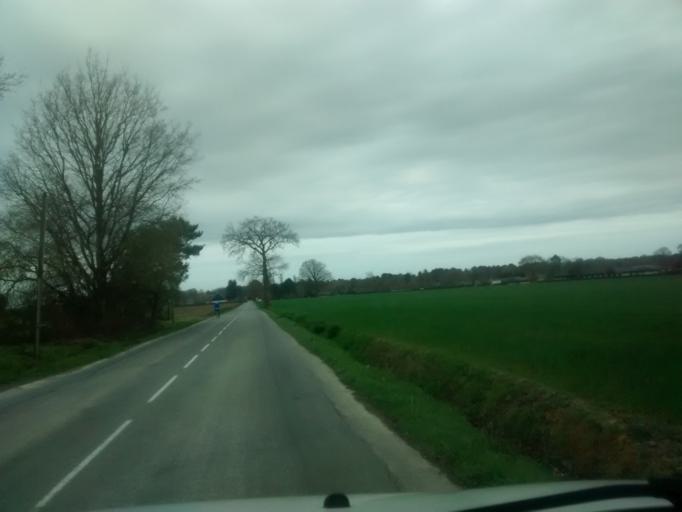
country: FR
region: Brittany
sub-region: Departement d'Ille-et-Vilaine
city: Fouillard
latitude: 48.1712
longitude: -1.5989
